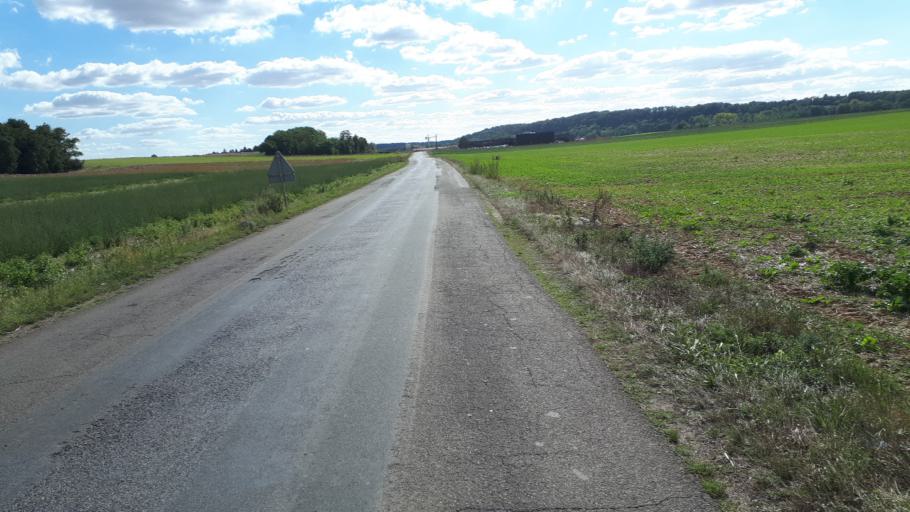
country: FR
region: Centre
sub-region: Departement du Loir-et-Cher
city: Villiers-sur-Loir
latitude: 47.8045
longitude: 0.9693
